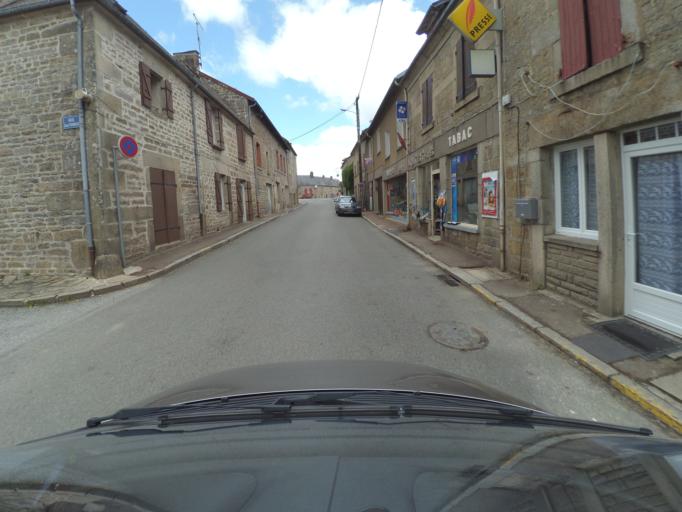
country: FR
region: Limousin
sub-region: Departement de la Haute-Vienne
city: Peyrat-le-Chateau
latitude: 45.8407
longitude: 1.9114
